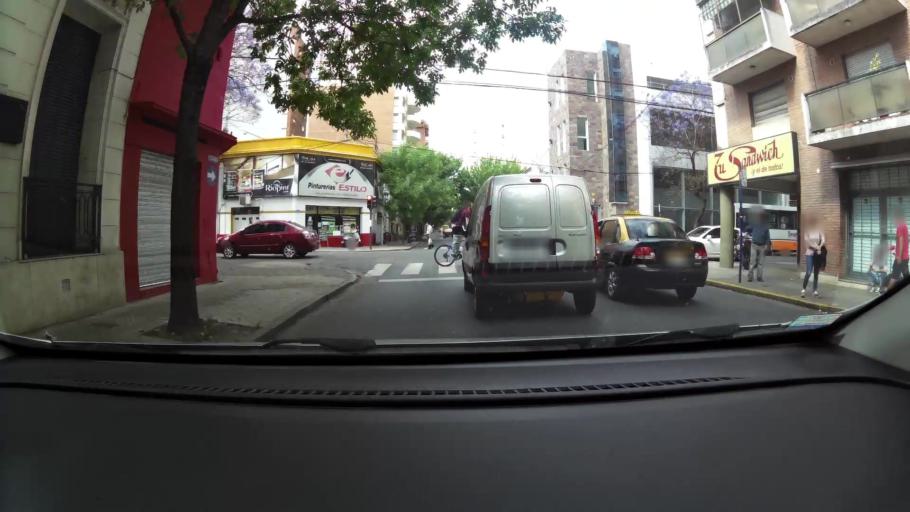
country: AR
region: Santa Fe
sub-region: Departamento de Rosario
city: Rosario
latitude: -32.9522
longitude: -60.6484
